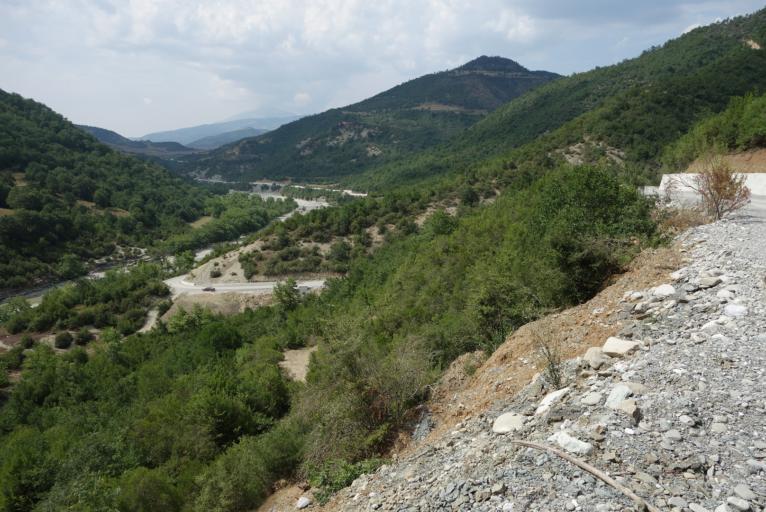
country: AL
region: Berat
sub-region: Rrethi i Skraparit
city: Cepan
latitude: 40.4375
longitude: 20.2817
